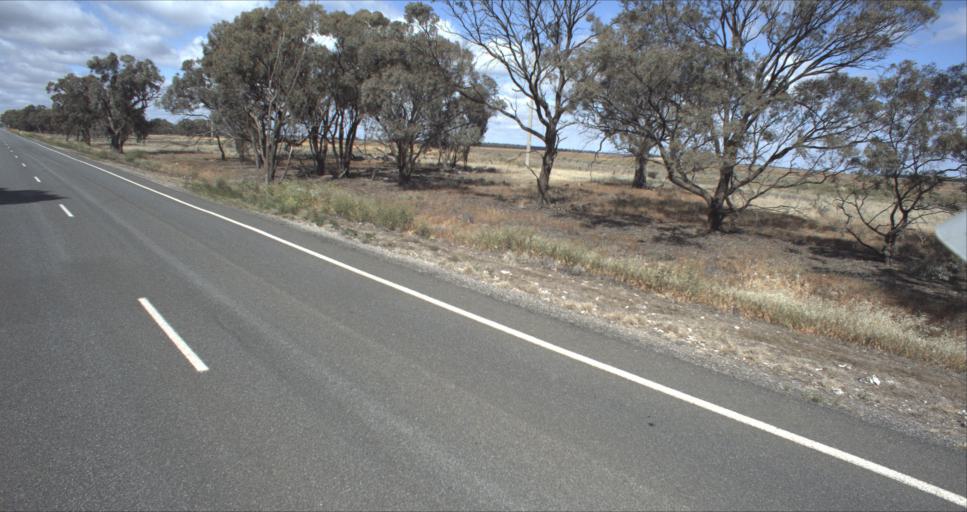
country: AU
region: New South Wales
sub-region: Murrumbidgee Shire
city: Darlington Point
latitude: -34.5594
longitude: 146.1693
